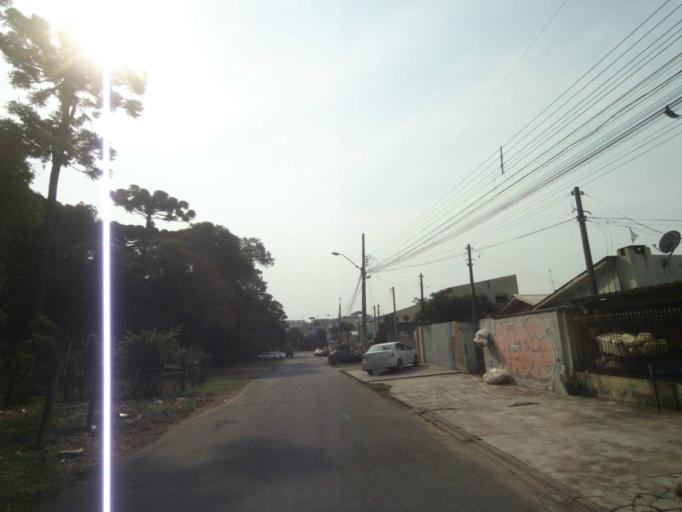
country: BR
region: Parana
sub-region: Sao Jose Dos Pinhais
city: Sao Jose dos Pinhais
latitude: -25.5239
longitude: -49.2754
